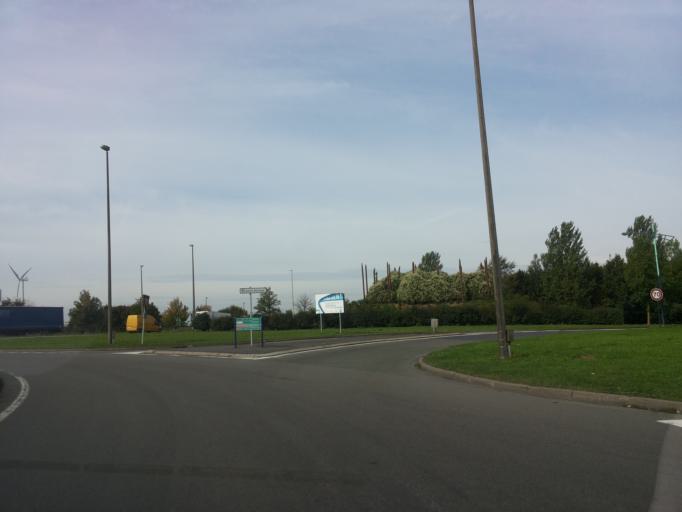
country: FR
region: Nord-Pas-de-Calais
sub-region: Departement du Pas-de-Calais
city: Feuchy
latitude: 50.2682
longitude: 2.8629
